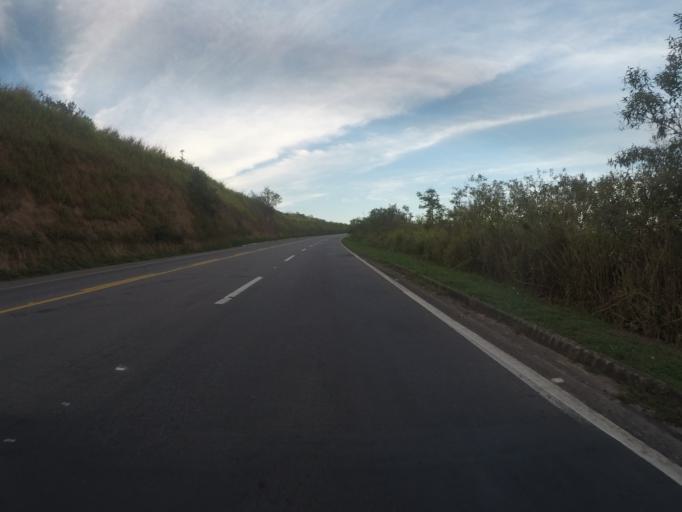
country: BR
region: Espirito Santo
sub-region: Aracruz
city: Aracruz
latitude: -19.6657
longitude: -40.2508
